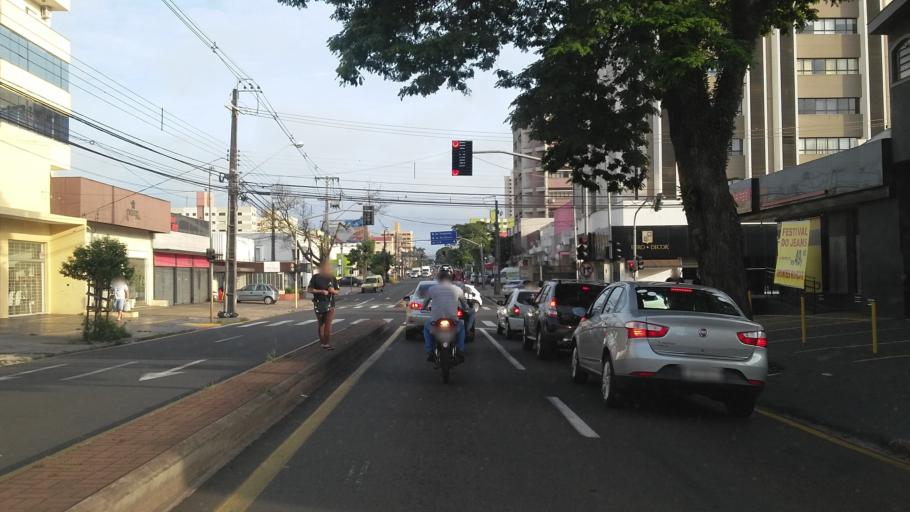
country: BR
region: Parana
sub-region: Londrina
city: Londrina
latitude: -23.3083
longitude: -51.1782
